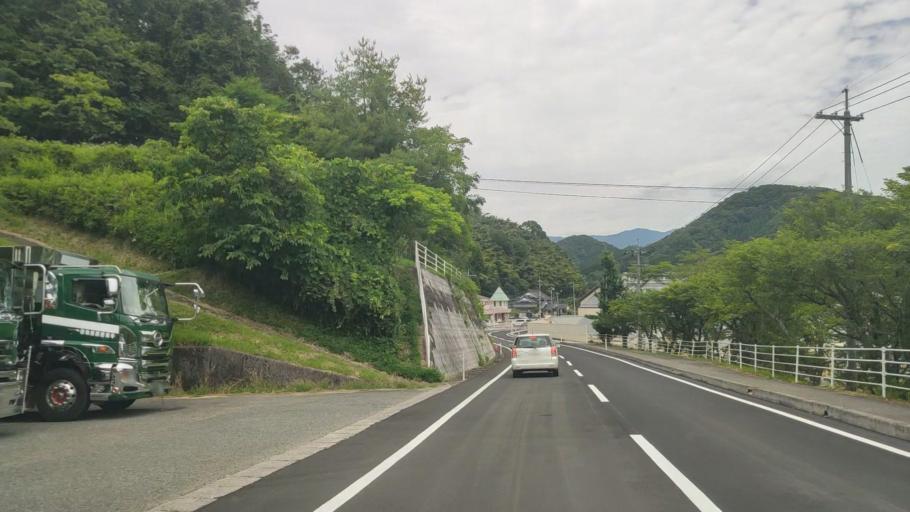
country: JP
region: Hyogo
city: Yamazakicho-nakabirose
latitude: 35.1030
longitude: 134.3226
